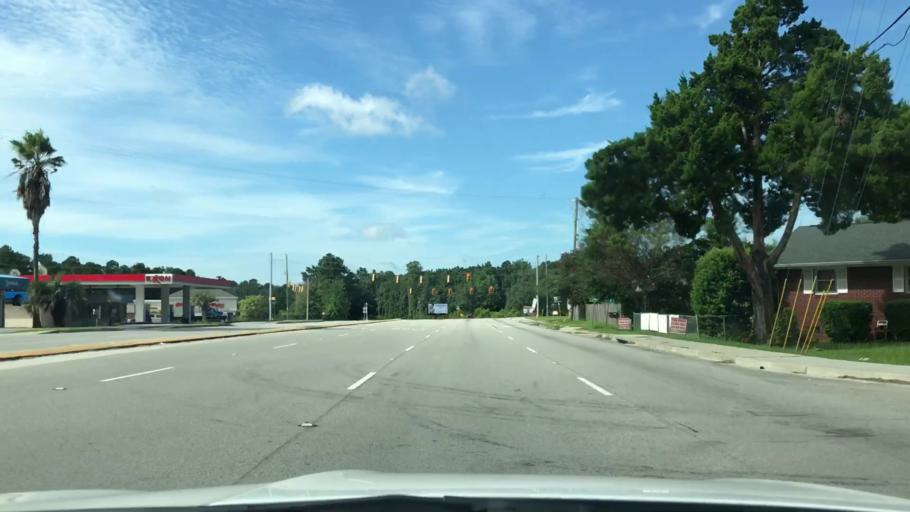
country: US
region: South Carolina
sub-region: Dorchester County
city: Centerville
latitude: 32.9689
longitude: -80.2003
